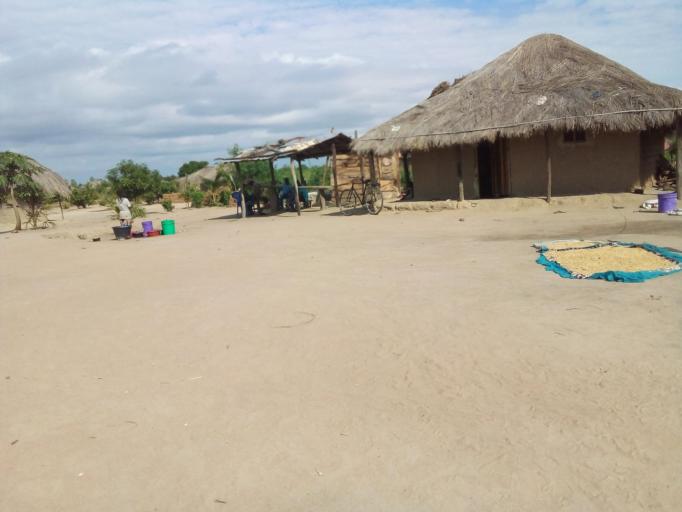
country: MZ
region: Zambezia
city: Quelimane
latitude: -17.5517
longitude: 36.7076
